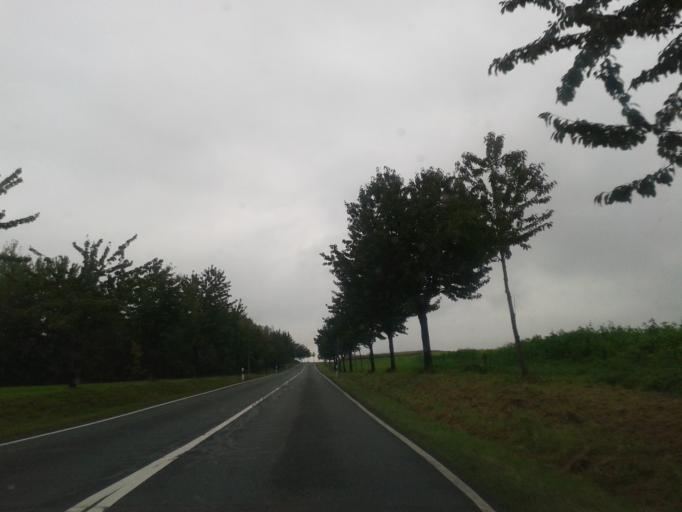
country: DE
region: Saxony
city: Reinsberg
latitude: 51.0393
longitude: 13.3469
